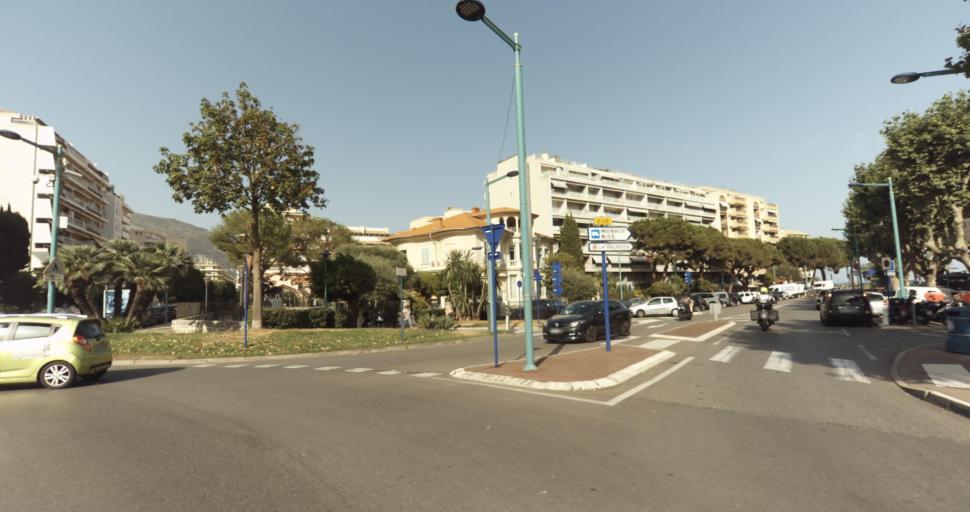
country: FR
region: Provence-Alpes-Cote d'Azur
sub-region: Departement des Alpes-Maritimes
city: Menton
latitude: 43.7715
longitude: 7.4928
